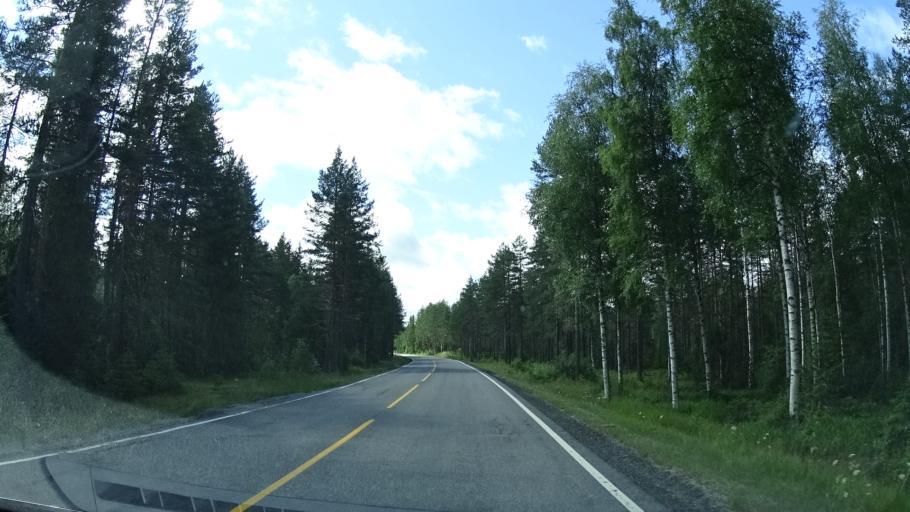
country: NO
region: Buskerud
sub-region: Krodsherad
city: Noresund
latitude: 60.2066
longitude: 9.8008
